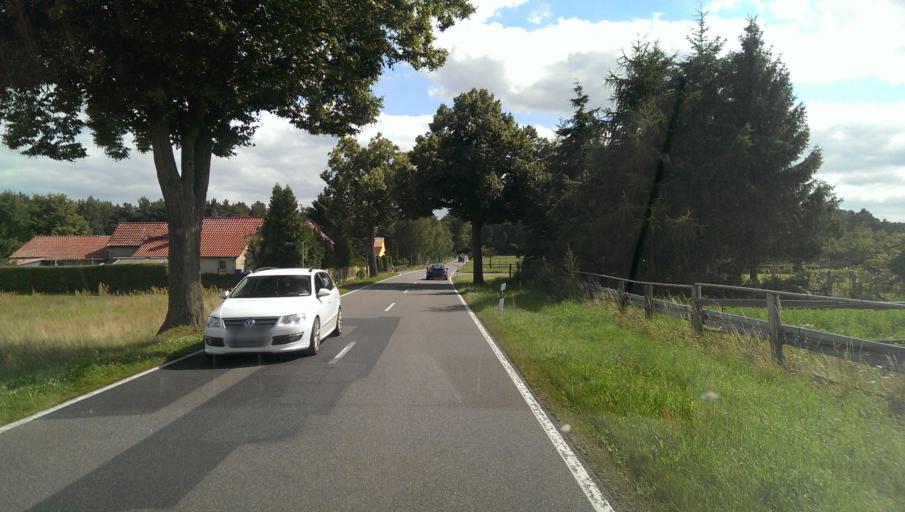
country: DE
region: Saxony-Anhalt
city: Nudersdorf
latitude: 51.9928
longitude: 12.5842
